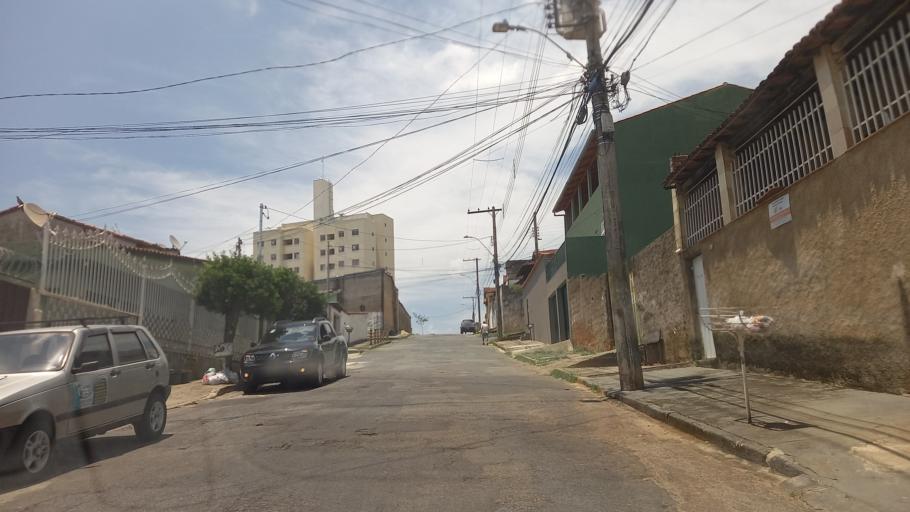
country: BR
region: Minas Gerais
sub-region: Contagem
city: Contagem
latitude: -19.9124
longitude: -44.0048
